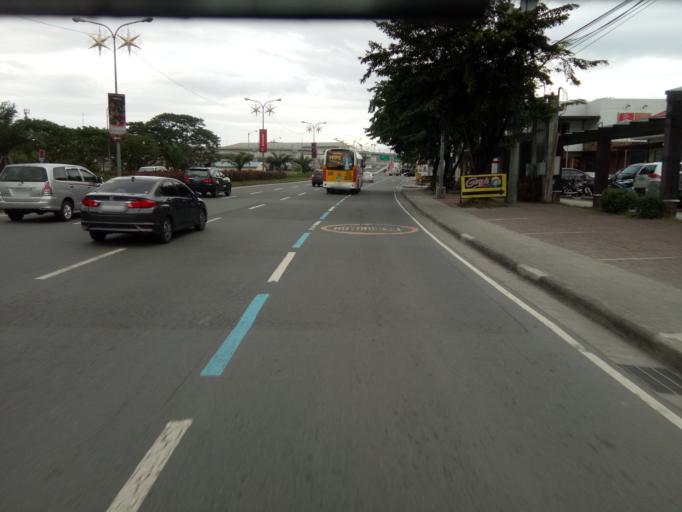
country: PH
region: Metro Manila
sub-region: Makati City
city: Makati City
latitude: 14.5212
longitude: 120.9907
